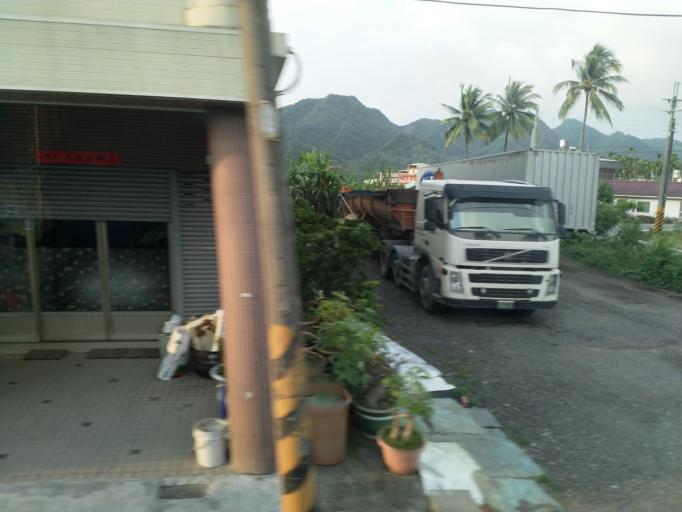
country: TW
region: Taiwan
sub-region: Pingtung
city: Pingtung
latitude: 22.8848
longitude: 120.5032
